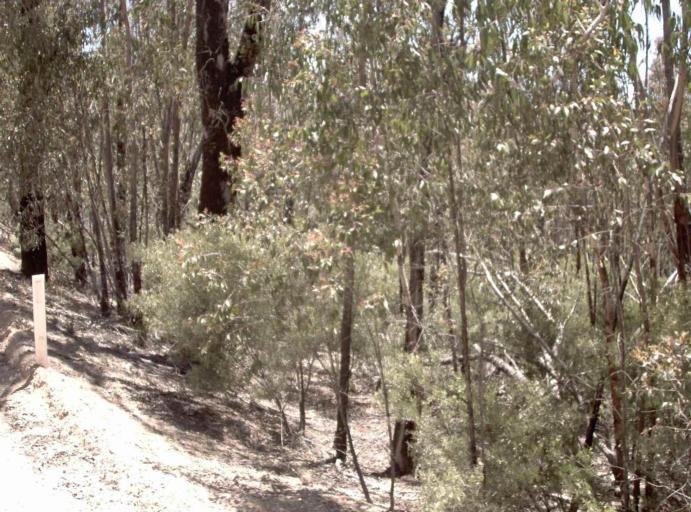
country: AU
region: New South Wales
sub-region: Snowy River
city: Jindabyne
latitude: -37.0829
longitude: 148.3294
